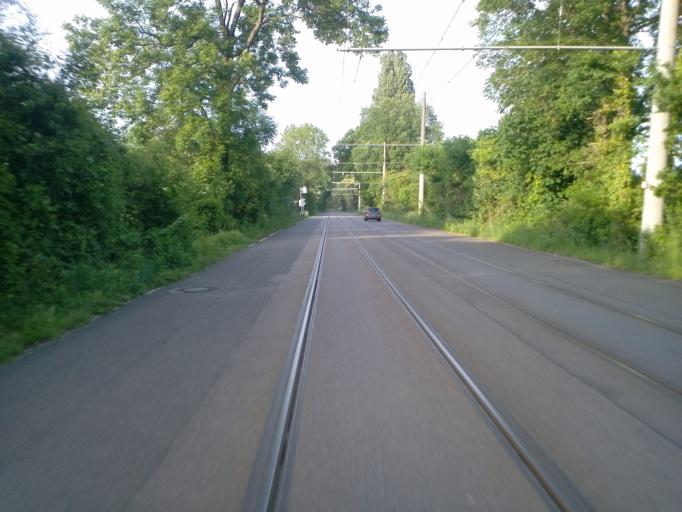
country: DE
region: Baden-Wuerttemberg
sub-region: Karlsruhe Region
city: Rheinstetten
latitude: 49.0022
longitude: 8.3155
